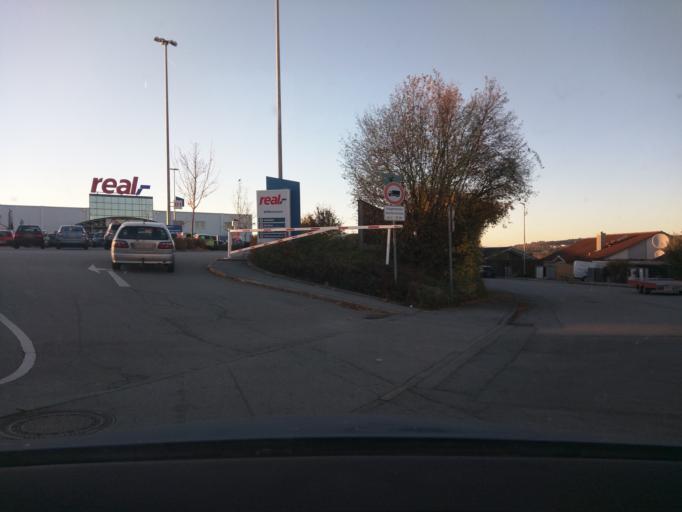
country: DE
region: Bavaria
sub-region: Lower Bavaria
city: Passau
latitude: 48.5750
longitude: 13.4045
